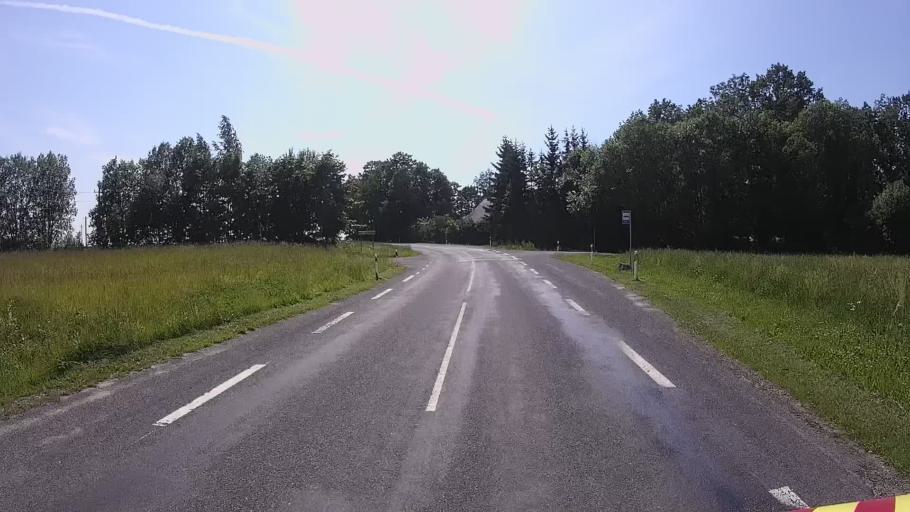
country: EE
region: Viljandimaa
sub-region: Karksi vald
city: Karksi-Nuia
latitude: 58.0725
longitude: 25.5563
